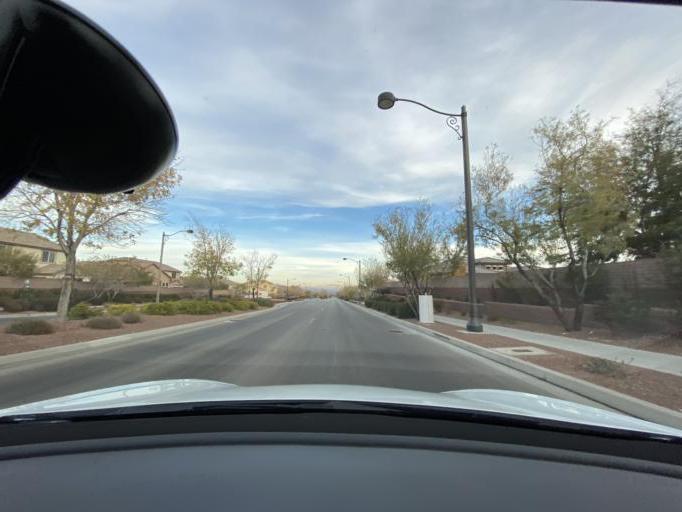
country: US
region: Nevada
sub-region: Clark County
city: Summerlin South
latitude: 36.2882
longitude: -115.3252
